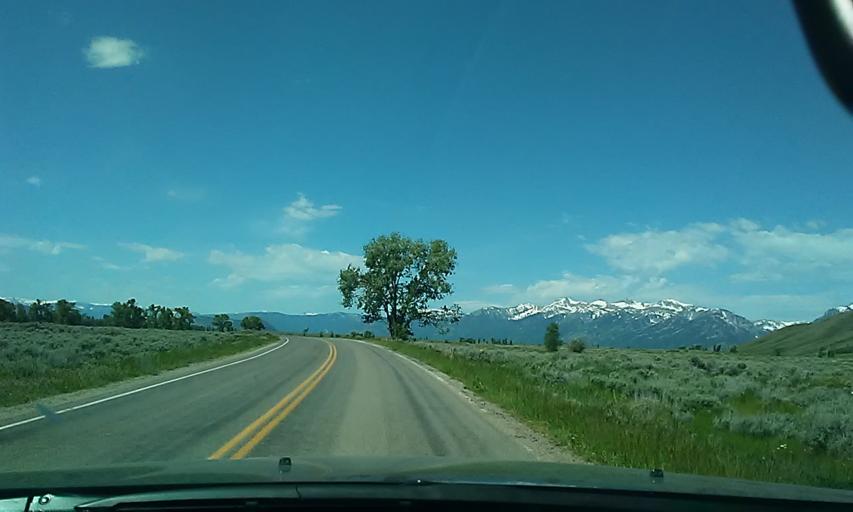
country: US
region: Wyoming
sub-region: Teton County
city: Jackson
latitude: 43.6244
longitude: -110.6645
